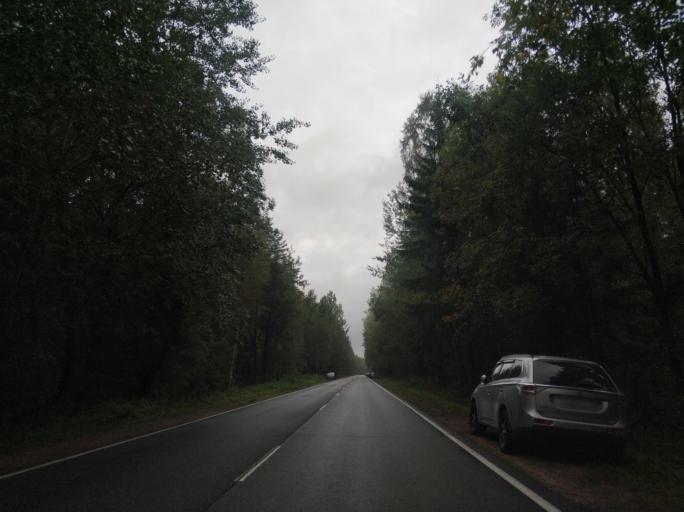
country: RU
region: Leningrad
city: Borisova Griva
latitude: 60.1554
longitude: 30.9306
